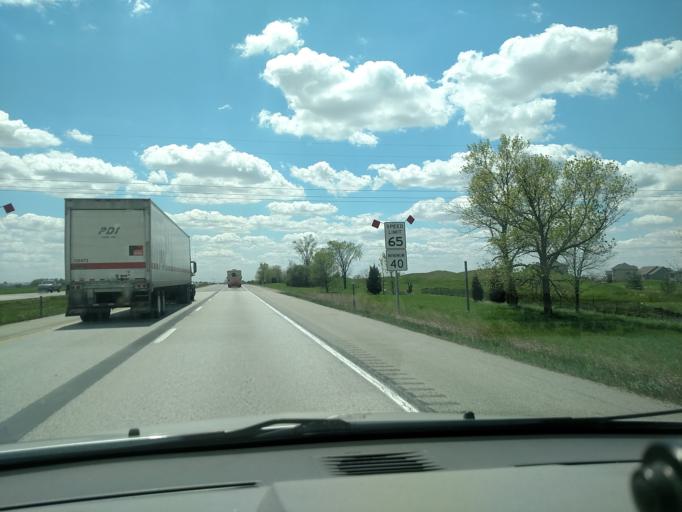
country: US
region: Iowa
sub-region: Polk County
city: Ankeny
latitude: 41.7730
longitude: -93.5708
